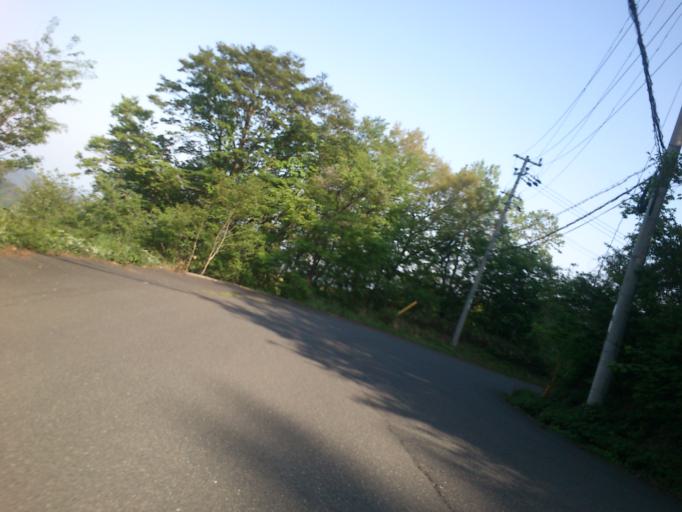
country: JP
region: Kyoto
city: Miyazu
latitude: 35.7171
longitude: 135.1945
